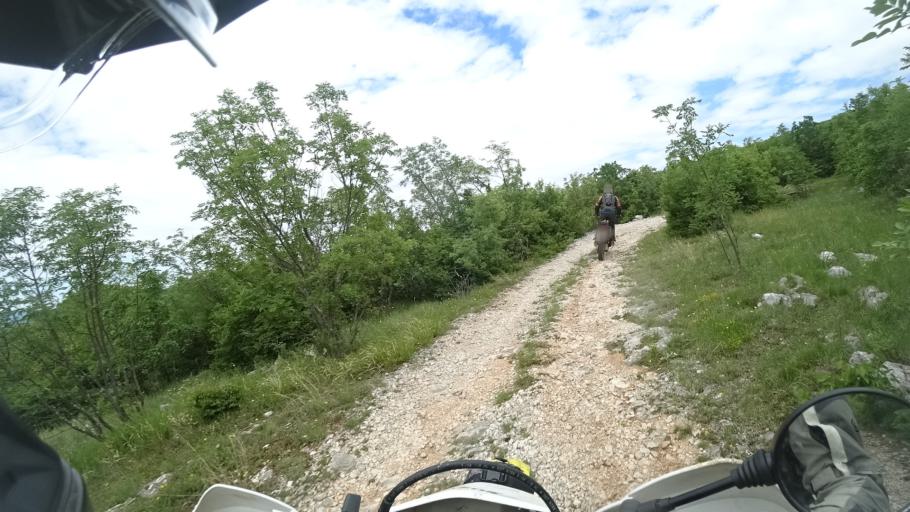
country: HR
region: Splitsko-Dalmatinska
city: Hrvace
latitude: 43.8927
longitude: 16.5367
